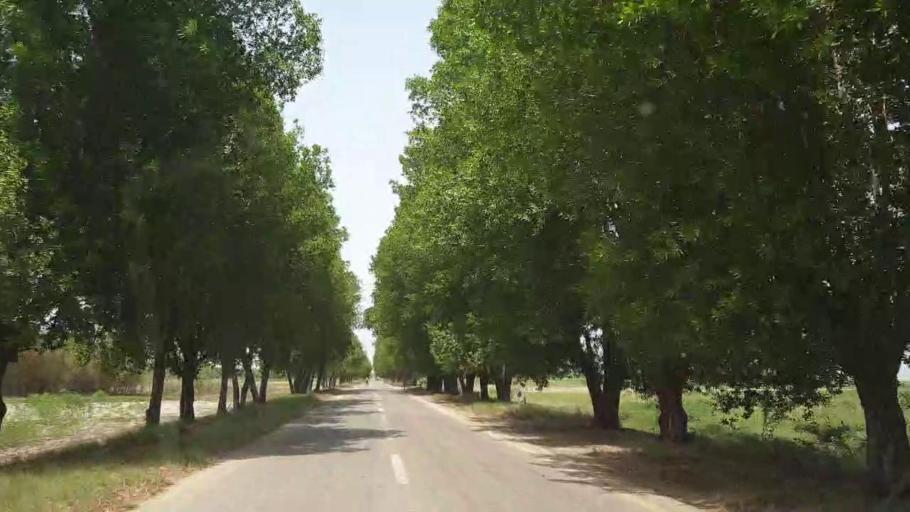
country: PK
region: Sindh
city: Sakrand
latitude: 26.1857
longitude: 68.2322
